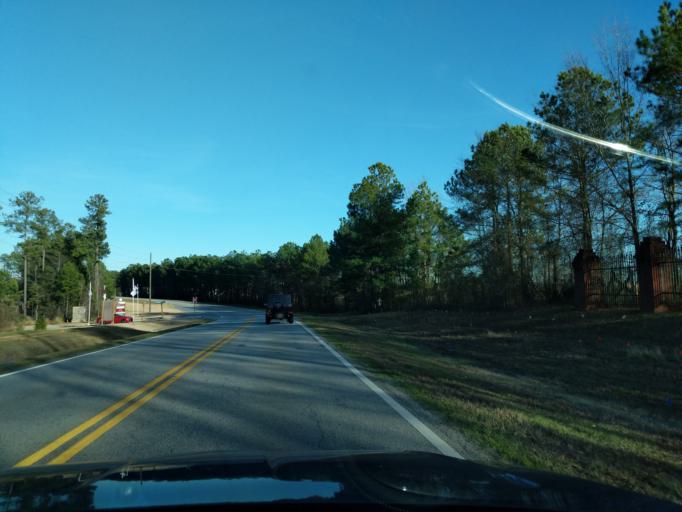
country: US
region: Georgia
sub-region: Columbia County
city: Evans
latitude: 33.5484
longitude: -82.2117
